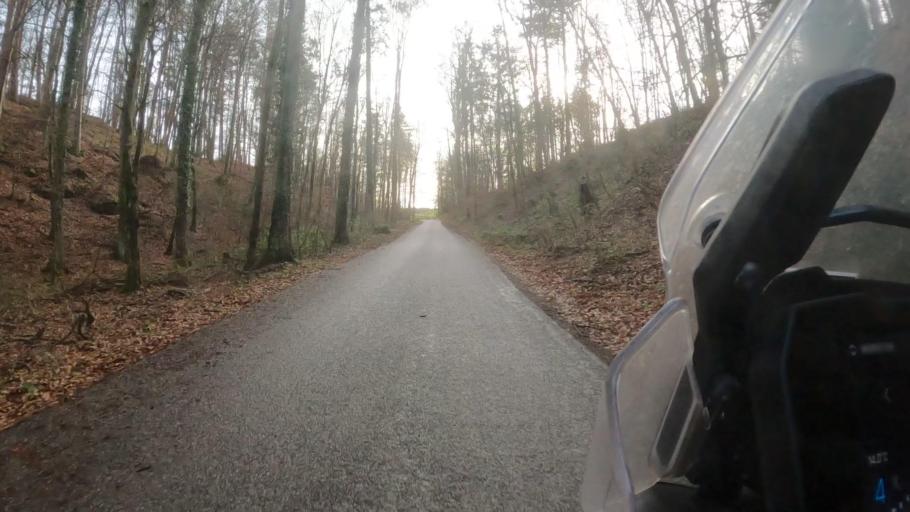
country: CH
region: Zurich
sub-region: Bezirk Buelach
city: Glattfelden
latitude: 47.5488
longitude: 8.5019
